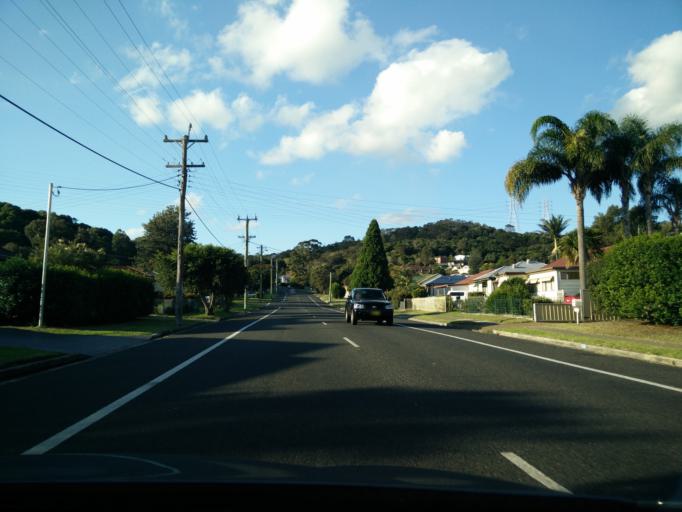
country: AU
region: New South Wales
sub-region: Wollongong
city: Berkeley
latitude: -34.4734
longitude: 150.8422
